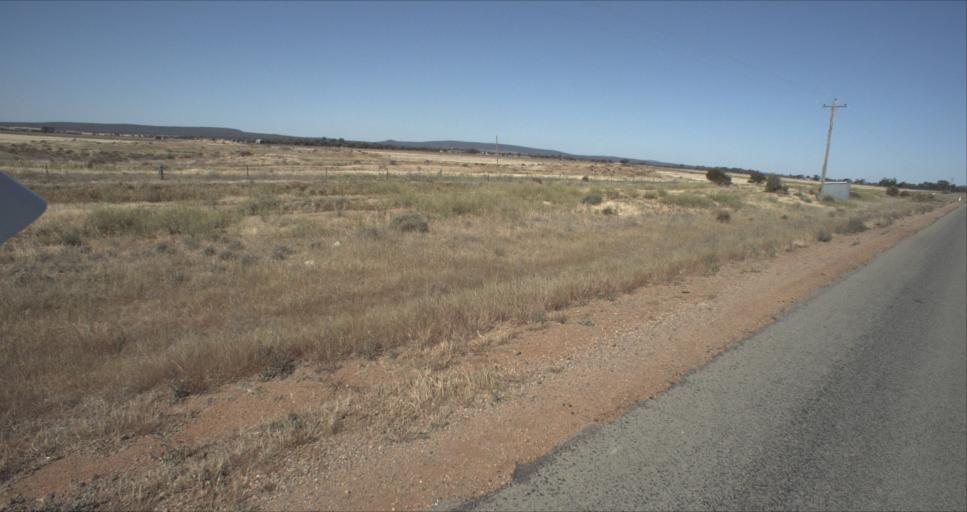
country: AU
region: New South Wales
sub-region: Leeton
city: Leeton
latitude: -34.4913
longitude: 146.3836
